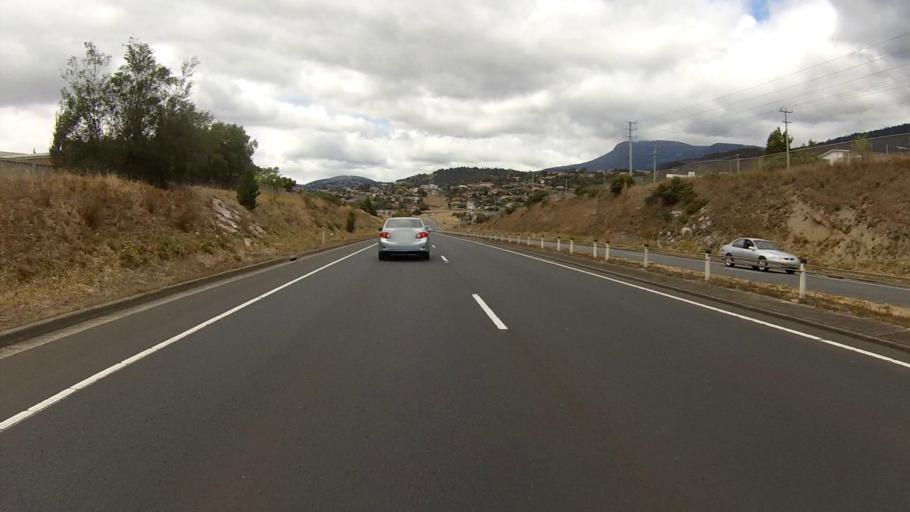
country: AU
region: Tasmania
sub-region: Glenorchy
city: Berriedale
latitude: -42.8094
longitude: 147.2497
